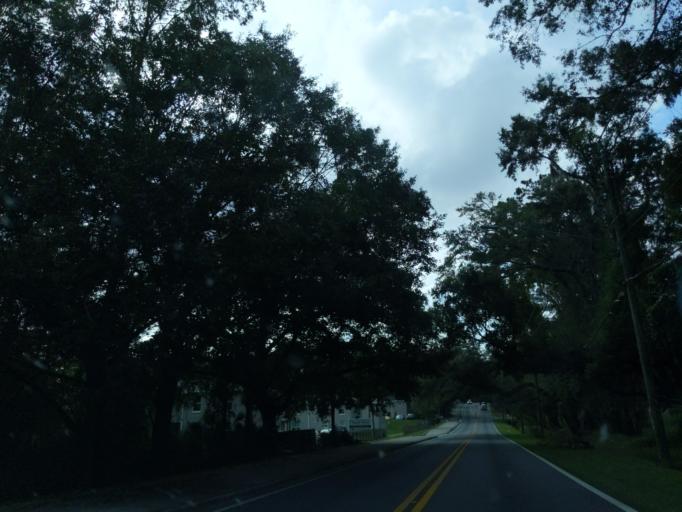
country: US
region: Florida
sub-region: Leon County
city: Tallahassee
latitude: 30.4200
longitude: -84.2745
